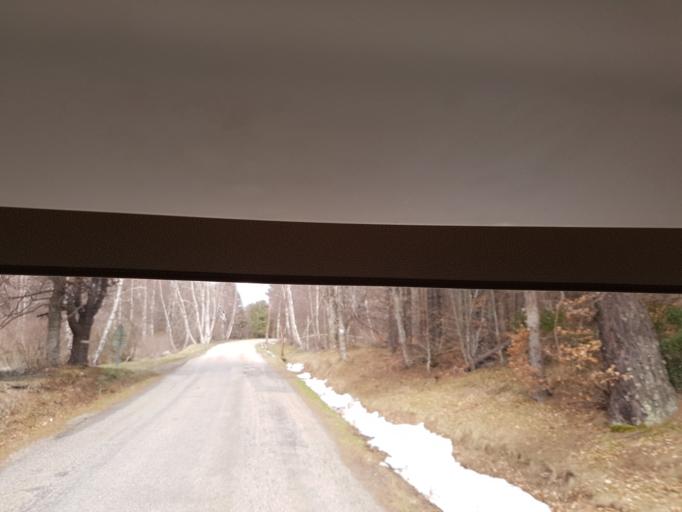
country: FR
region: Languedoc-Roussillon
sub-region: Departement de l'Aude
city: Quillan
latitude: 42.6825
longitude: 2.1188
